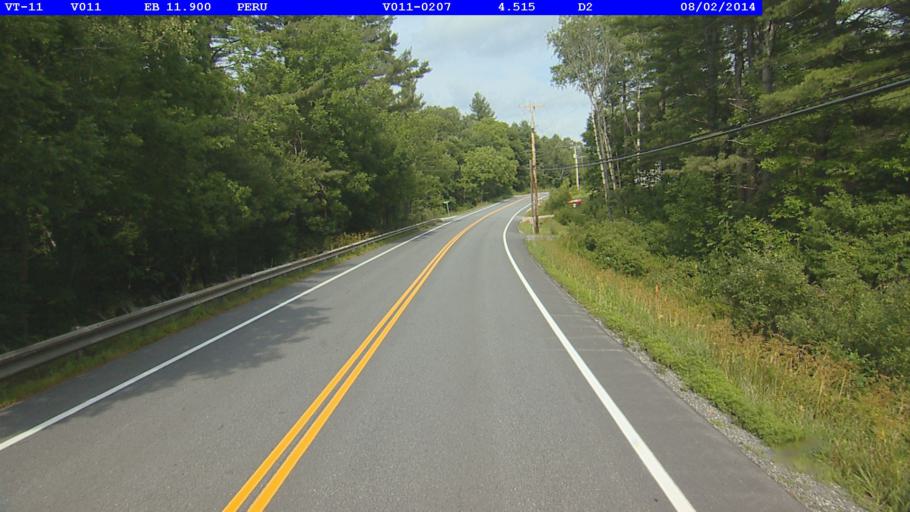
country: US
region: Vermont
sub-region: Bennington County
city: Manchester Center
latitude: 43.2361
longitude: -72.8675
